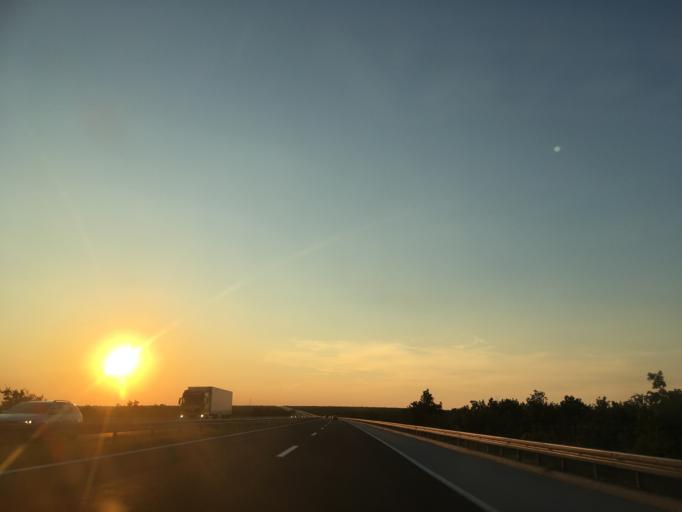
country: HR
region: Zadarska
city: Benkovac
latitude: 43.9885
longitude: 15.6265
